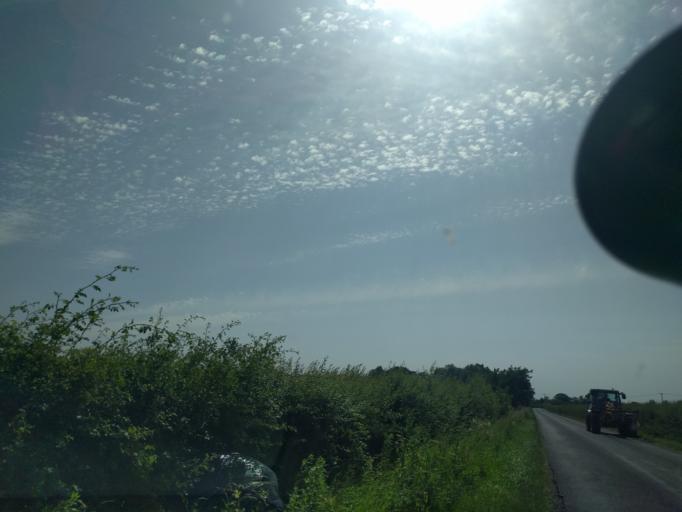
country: GB
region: England
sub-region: Wiltshire
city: Lyneham
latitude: 51.5396
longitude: -1.9765
